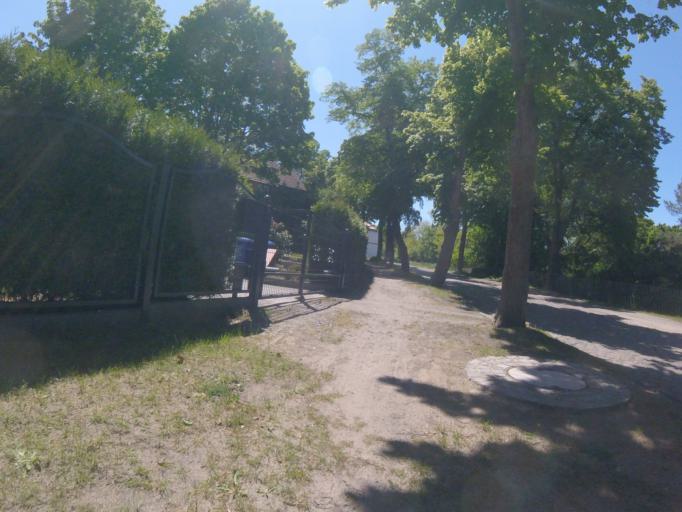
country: DE
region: Brandenburg
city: Teupitz
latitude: 52.1335
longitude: 13.6219
